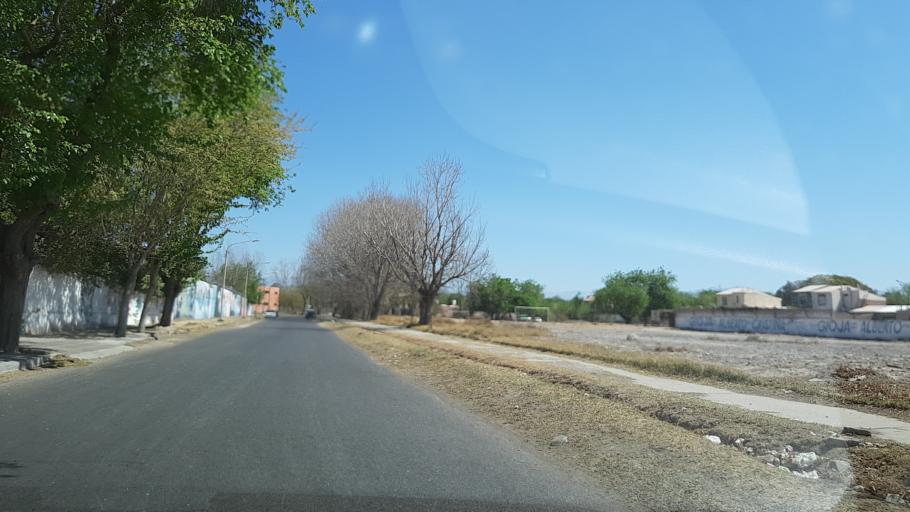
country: AR
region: San Juan
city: San Juan
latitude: -31.5261
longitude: -68.5416
